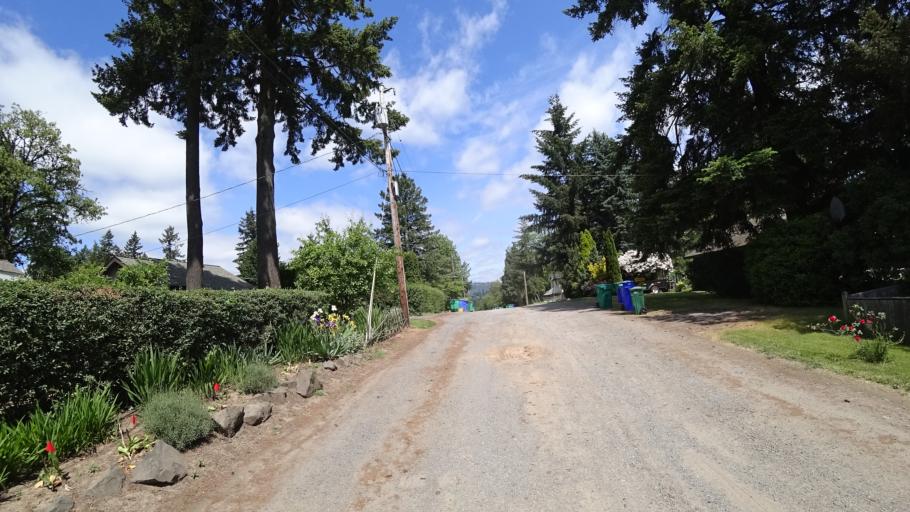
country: US
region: Oregon
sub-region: Washington County
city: Garden Home-Whitford
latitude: 45.4624
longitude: -122.7194
